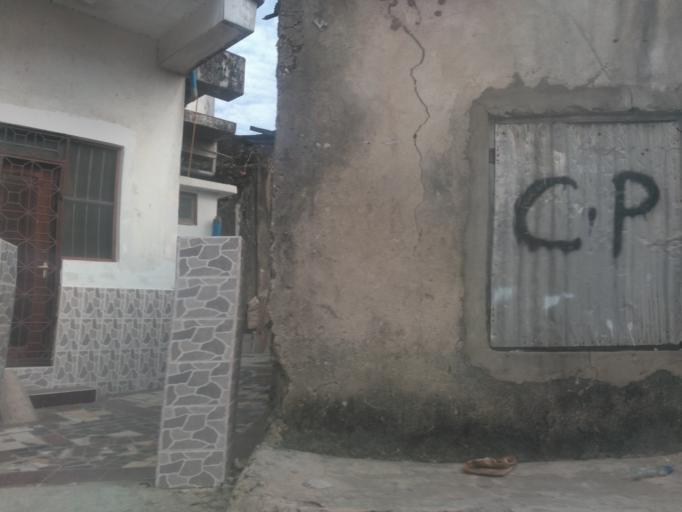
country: TZ
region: Zanzibar Urban/West
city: Zanzibar
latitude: -6.1589
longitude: 39.2025
